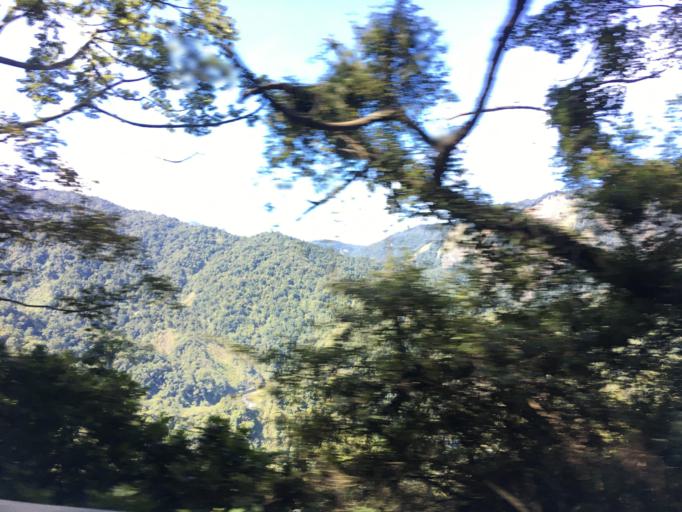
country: TW
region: Taiwan
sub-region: Yilan
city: Yilan
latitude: 24.5495
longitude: 121.5103
